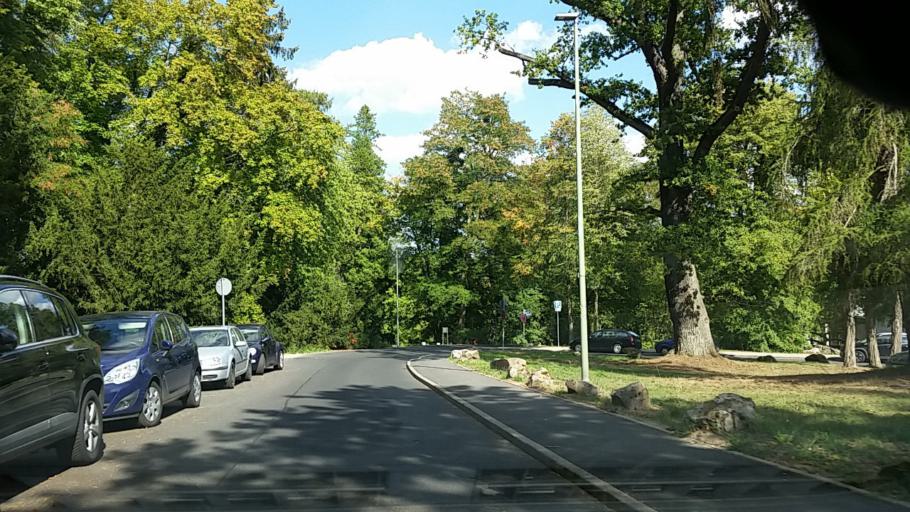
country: DE
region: Hesse
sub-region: Regierungsbezirk Kassel
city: Baunatal
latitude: 51.3138
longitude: 9.4232
